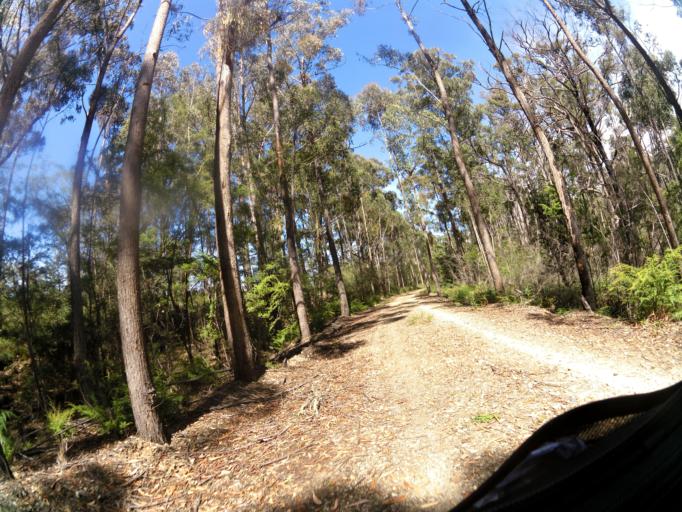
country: AU
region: Victoria
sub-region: East Gippsland
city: Lakes Entrance
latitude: -37.7191
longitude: 148.1279
